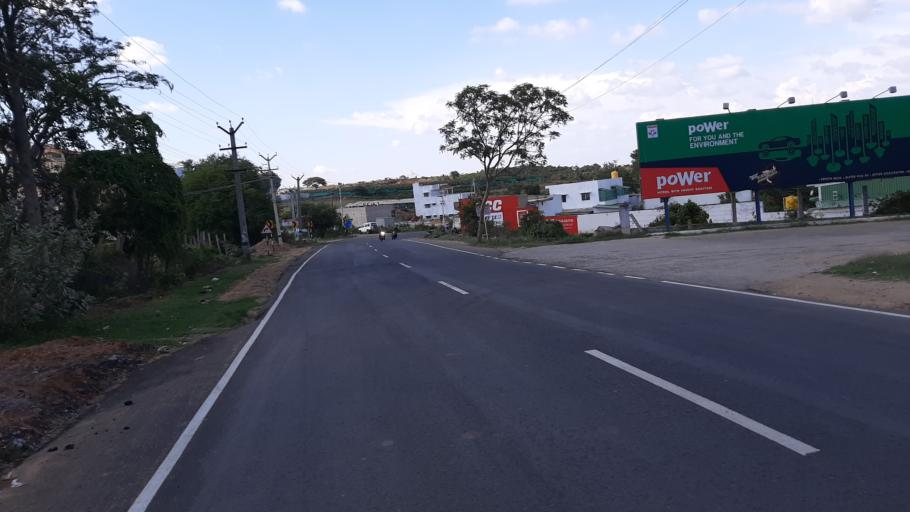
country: IN
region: Tamil Nadu
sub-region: Krishnagiri
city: Denkanikota
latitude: 12.5341
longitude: 77.7878
